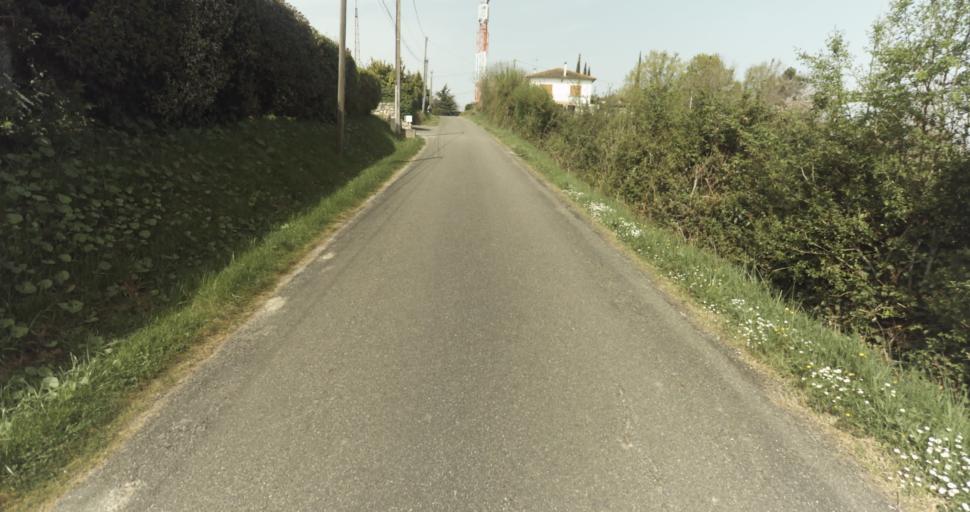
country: FR
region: Midi-Pyrenees
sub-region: Departement du Tarn-et-Garonne
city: Moissac
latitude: 44.1086
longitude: 1.0742
